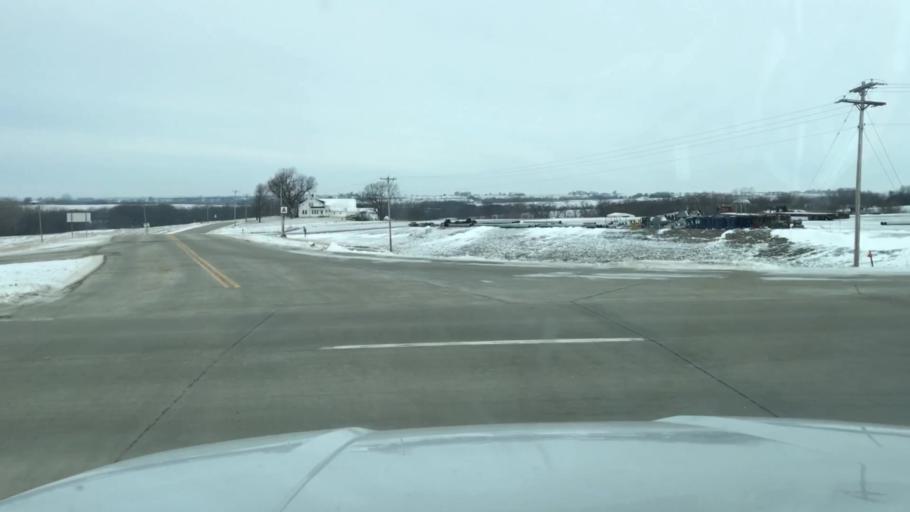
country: US
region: Missouri
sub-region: Andrew County
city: Savannah
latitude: 40.0252
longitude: -94.8799
